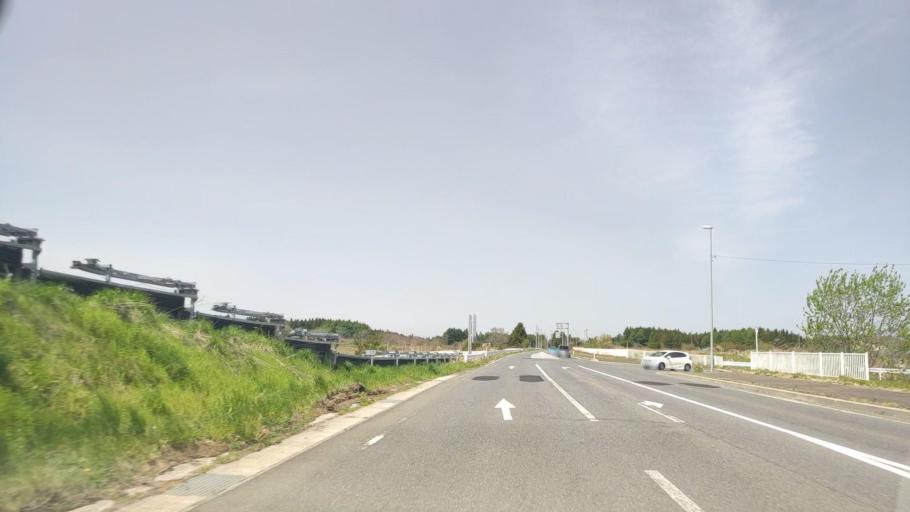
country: JP
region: Aomori
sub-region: Hachinohe Shi
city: Uchimaru
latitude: 40.5277
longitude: 141.4090
